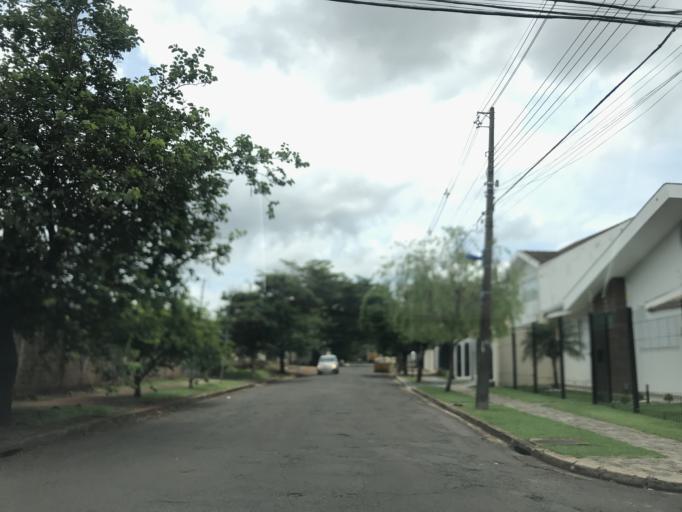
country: BR
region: Parana
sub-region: Maringa
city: Maringa
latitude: -23.4490
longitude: -51.9570
